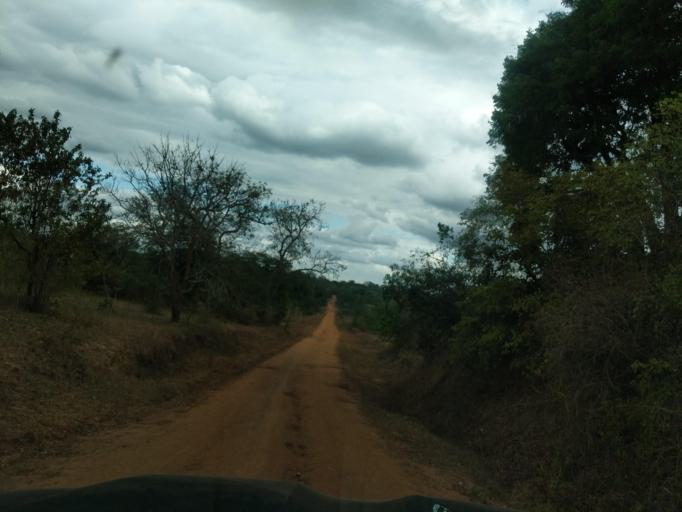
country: TZ
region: Pwani
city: Mvomero
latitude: -5.9350
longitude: 38.4204
